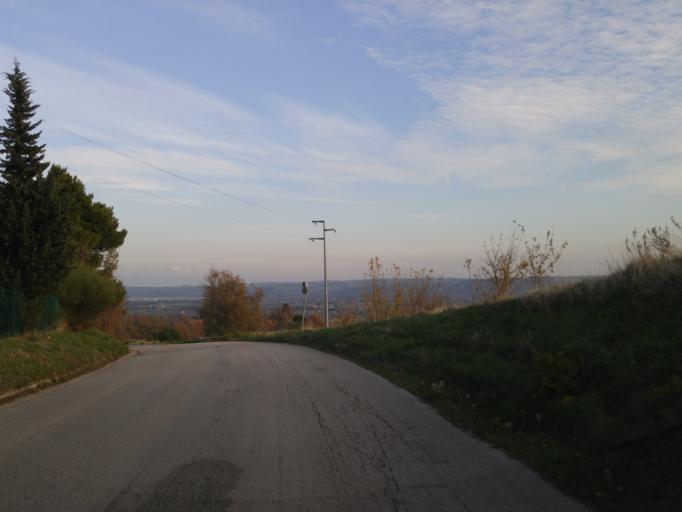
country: IT
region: The Marches
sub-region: Provincia di Pesaro e Urbino
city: Lucrezia
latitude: 43.7935
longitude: 12.9379
